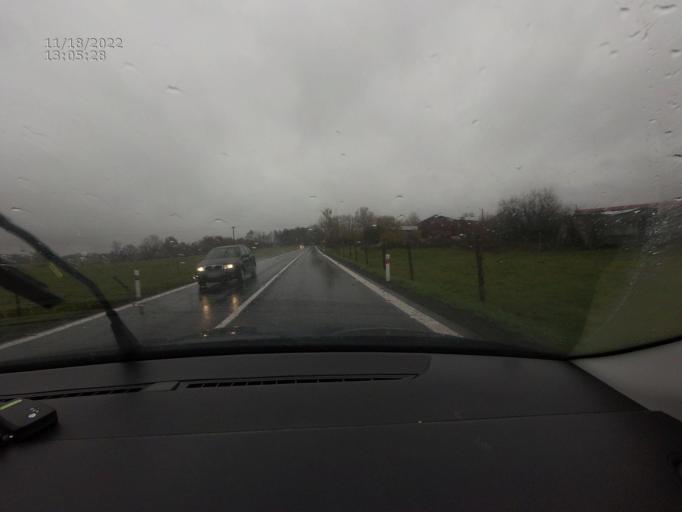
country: CZ
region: Plzensky
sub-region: Okres Klatovy
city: Planice
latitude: 49.3415
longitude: 13.4836
